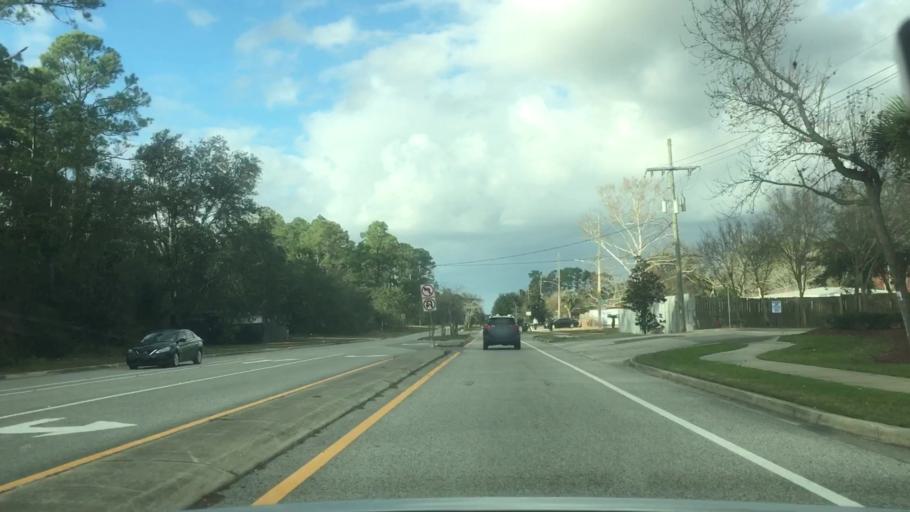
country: US
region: Florida
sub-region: Duval County
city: Neptune Beach
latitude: 30.2878
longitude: -81.5048
